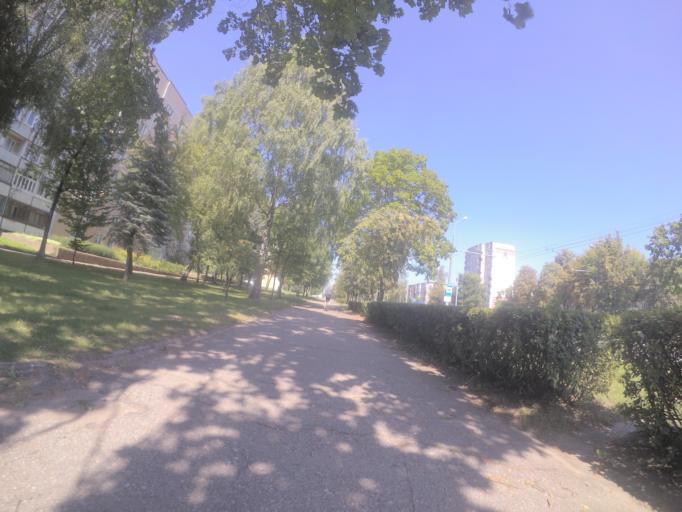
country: BY
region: Grodnenskaya
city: Hrodna
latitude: 53.6671
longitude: 23.8010
